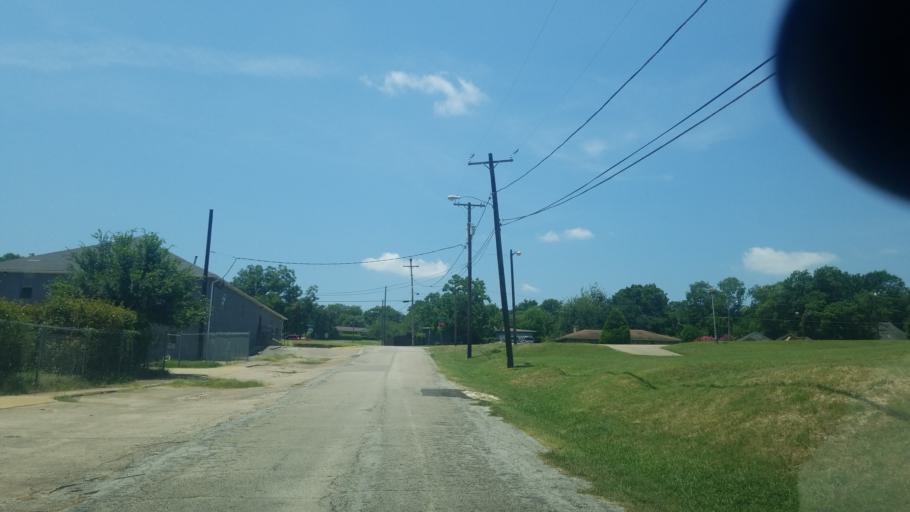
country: US
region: Texas
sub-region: Dallas County
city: Dallas
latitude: 32.7295
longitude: -96.7912
